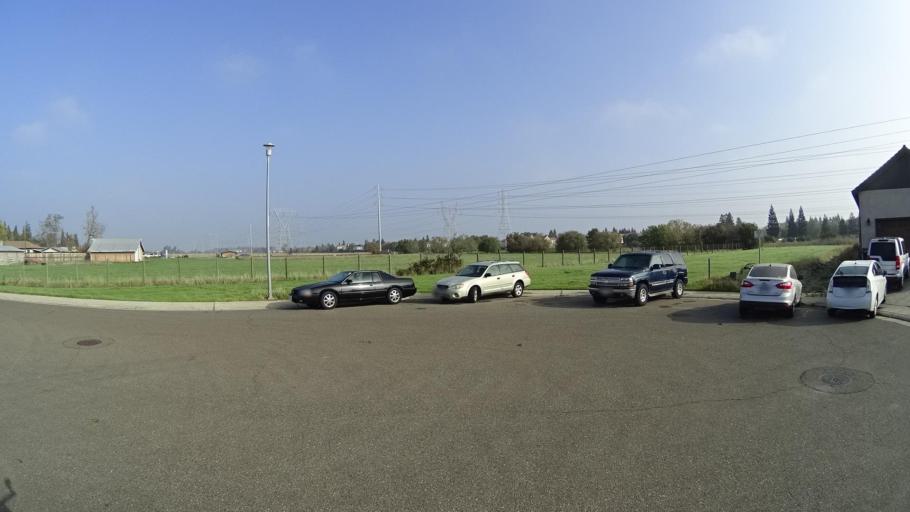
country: US
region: California
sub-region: Sacramento County
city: Elk Grove
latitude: 38.4107
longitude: -121.3519
